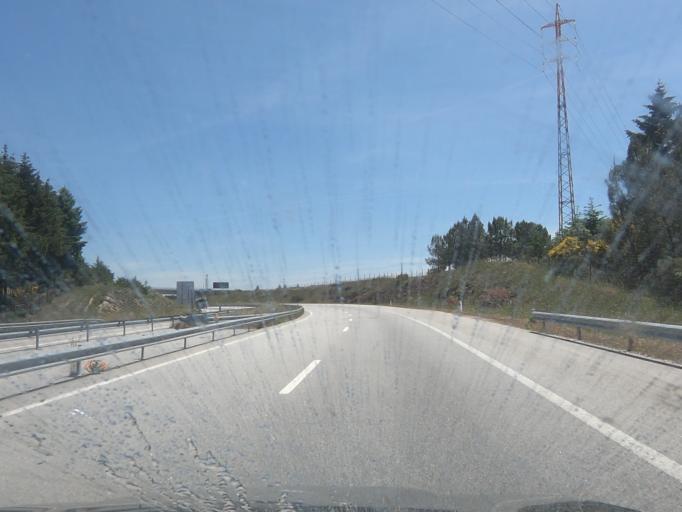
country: PT
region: Guarda
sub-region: Guarda
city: Sequeira
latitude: 40.5620
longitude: -7.2277
